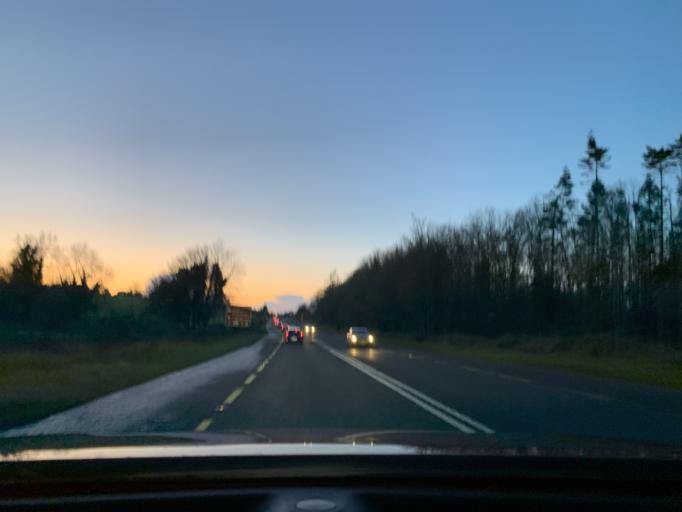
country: IE
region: Connaught
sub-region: Roscommon
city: Boyle
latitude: 53.9698
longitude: -8.2410
